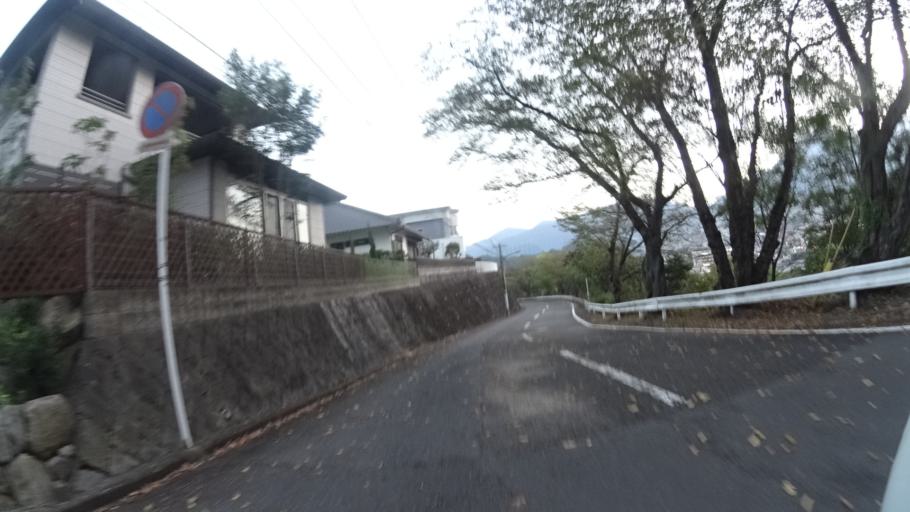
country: JP
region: Oita
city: Beppu
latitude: 33.3152
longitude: 131.4859
